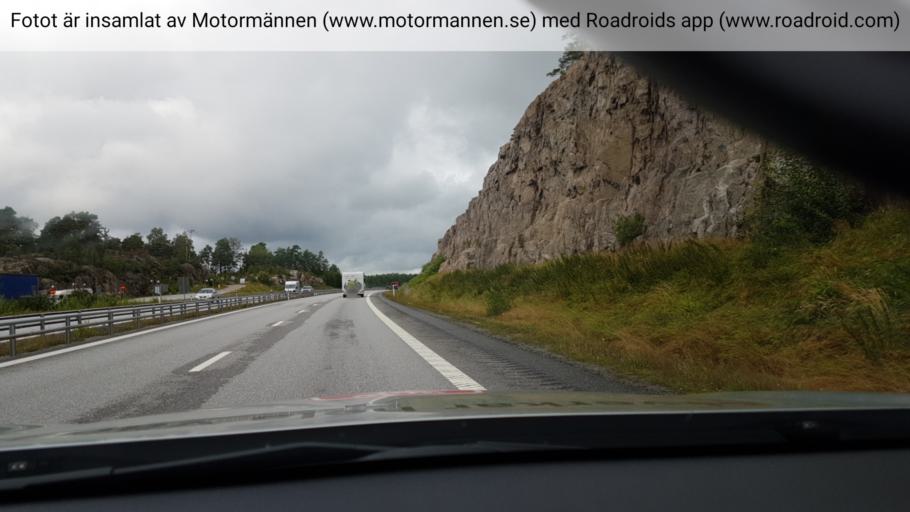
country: SE
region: Vaestra Goetaland
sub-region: Stromstads Kommun
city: Stroemstad
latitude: 59.0015
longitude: 11.2320
